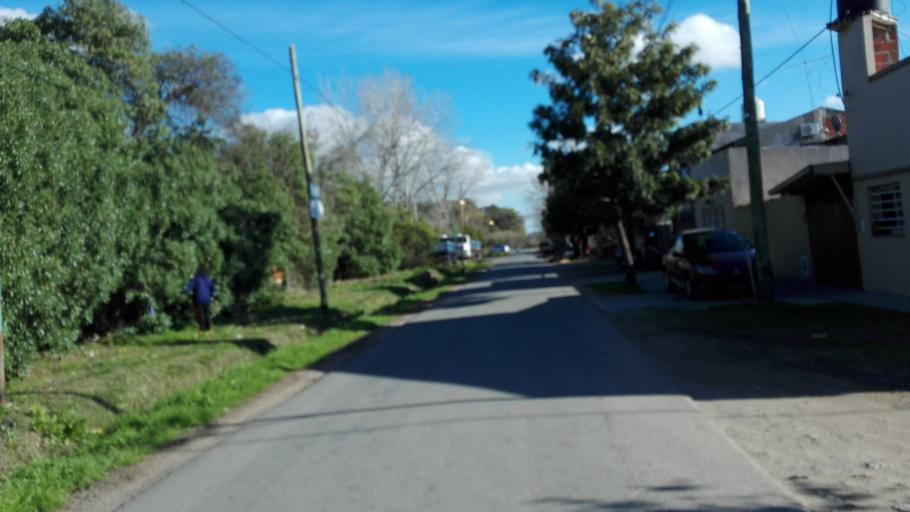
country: AR
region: Buenos Aires
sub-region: Partido de La Plata
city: La Plata
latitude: -34.8992
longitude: -58.0230
